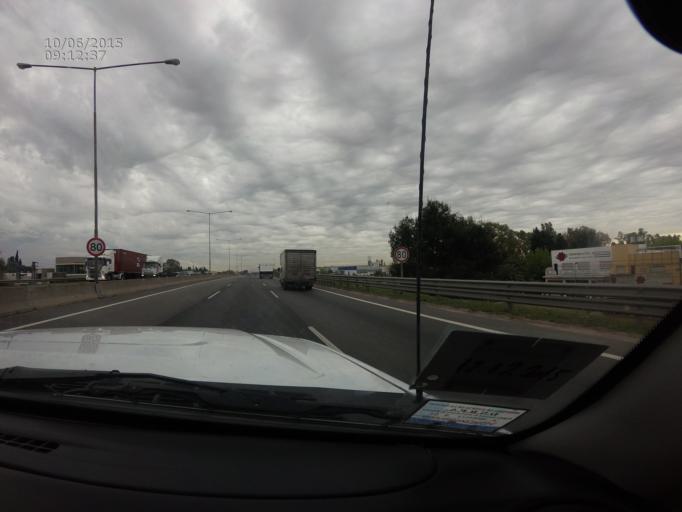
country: AR
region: Buenos Aires
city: Belen de Escobar
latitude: -34.3487
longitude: -58.8073
